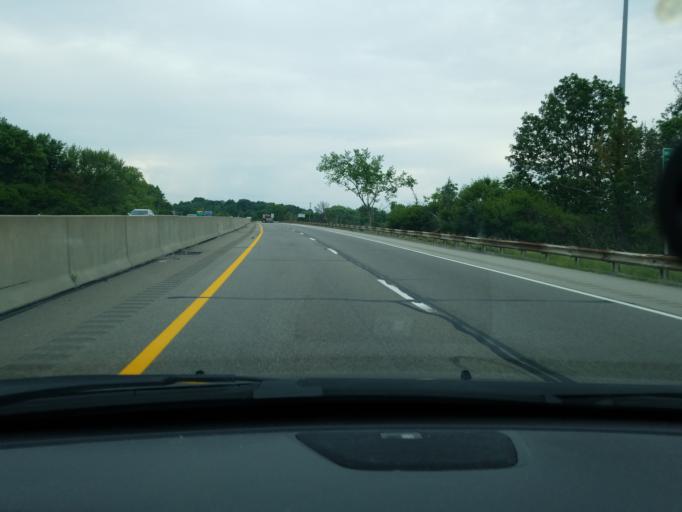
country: US
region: Ohio
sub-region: Mahoning County
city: New Middletown
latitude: 40.9136
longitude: -80.5226
